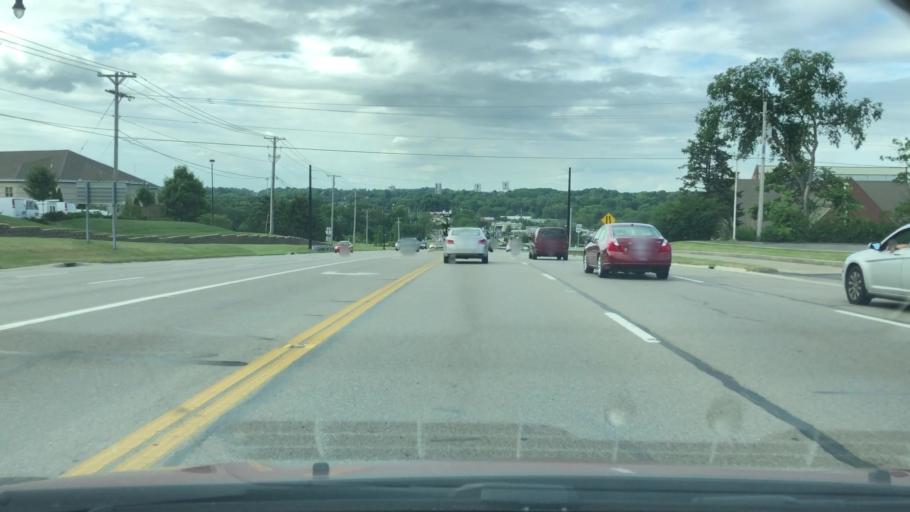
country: US
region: Ohio
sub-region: Montgomery County
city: Centerville
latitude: 39.6495
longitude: -84.1571
